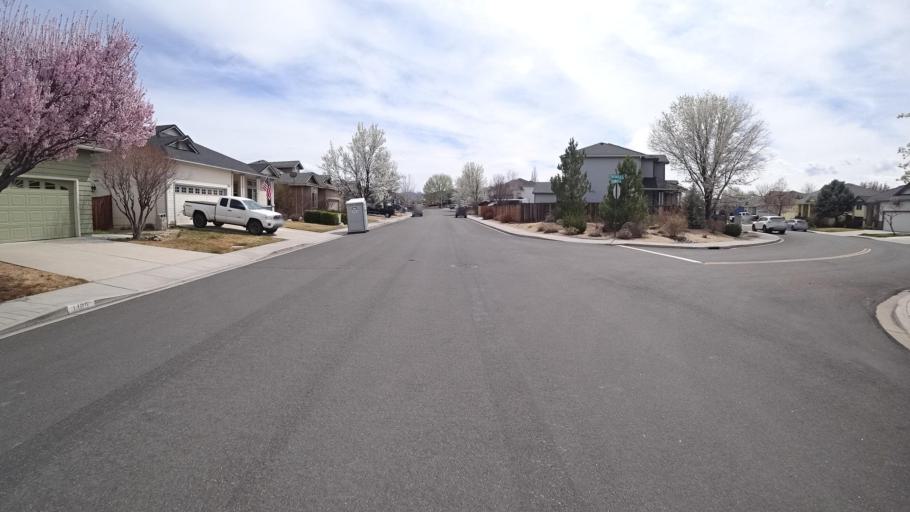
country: US
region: Nevada
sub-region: Washoe County
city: Sparks
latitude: 39.4574
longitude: -119.7617
